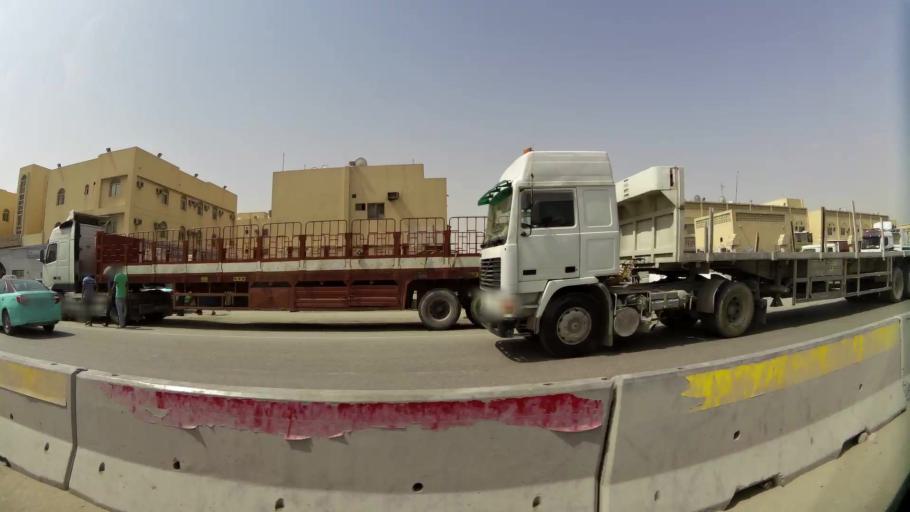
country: QA
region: Baladiyat ar Rayyan
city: Ar Rayyan
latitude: 25.1961
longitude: 51.4310
